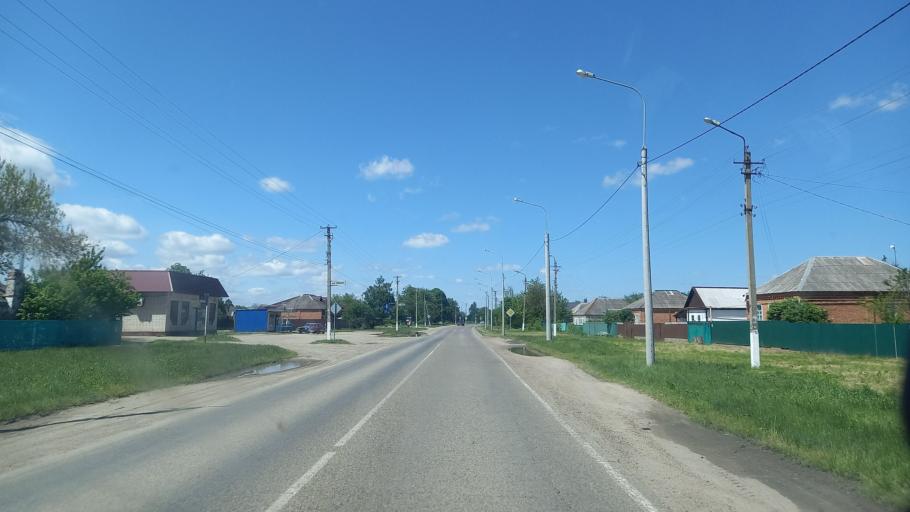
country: RU
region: Krasnodarskiy
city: Novoukrainskoye
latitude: 45.3802
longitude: 40.5397
